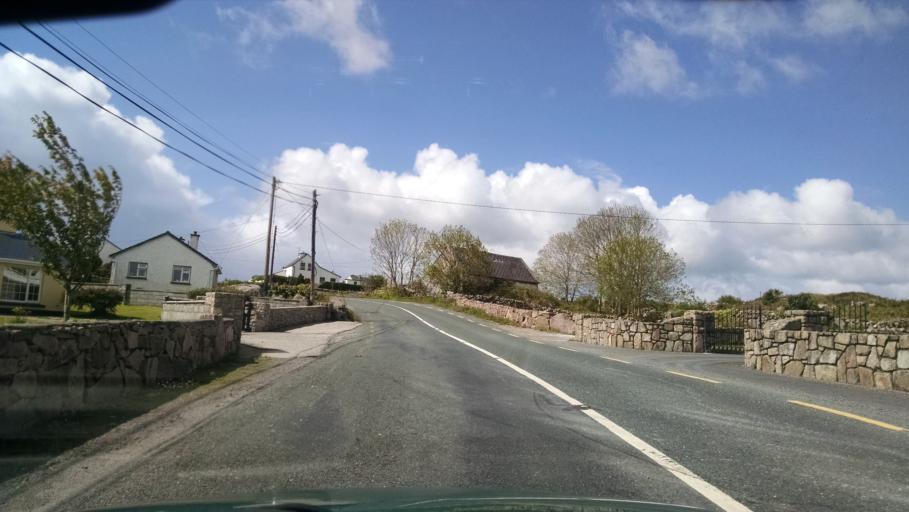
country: IE
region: Connaught
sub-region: County Galway
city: Oughterard
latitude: 53.2873
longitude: -9.5645
